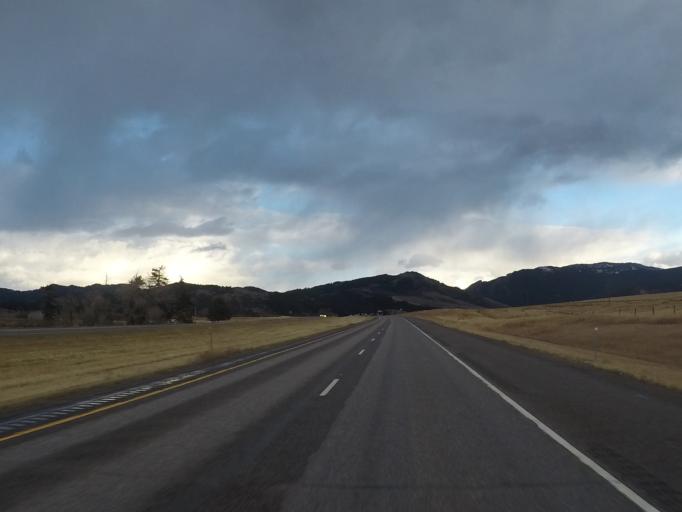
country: US
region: Montana
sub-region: Gallatin County
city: Bozeman
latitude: 45.6649
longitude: -110.9757
